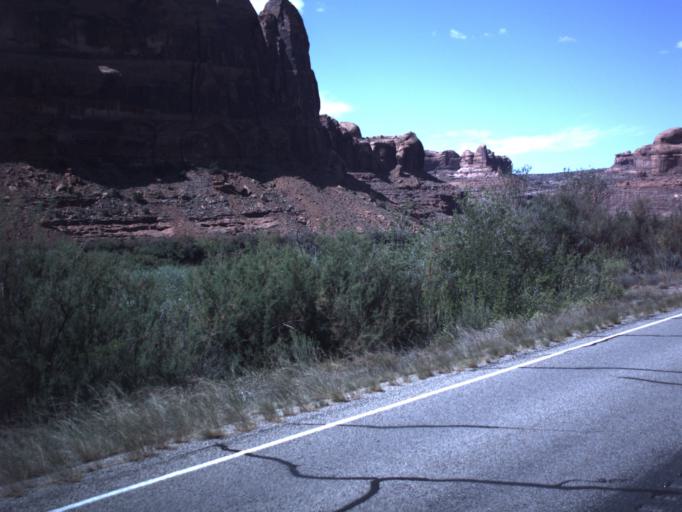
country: US
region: Utah
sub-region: Grand County
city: Moab
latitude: 38.5683
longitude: -109.6321
